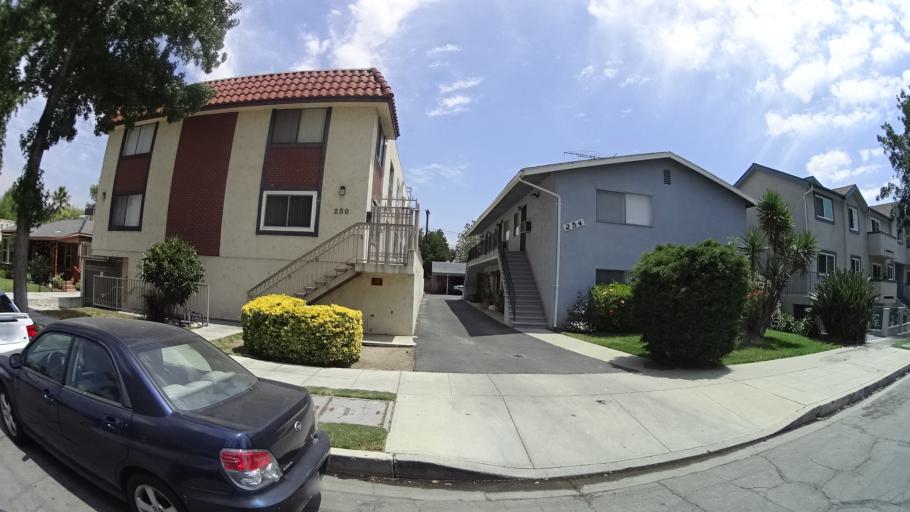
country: US
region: California
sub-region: Los Angeles County
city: Burbank
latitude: 34.1693
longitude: -118.3093
